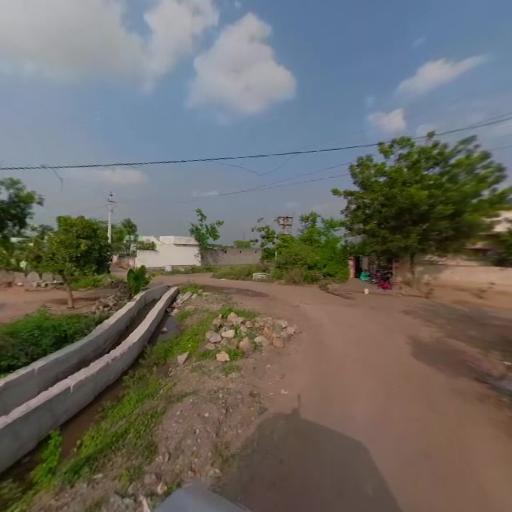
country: IN
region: Telangana
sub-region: Nalgonda
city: Suriapet
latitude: 17.1667
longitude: 79.5074
